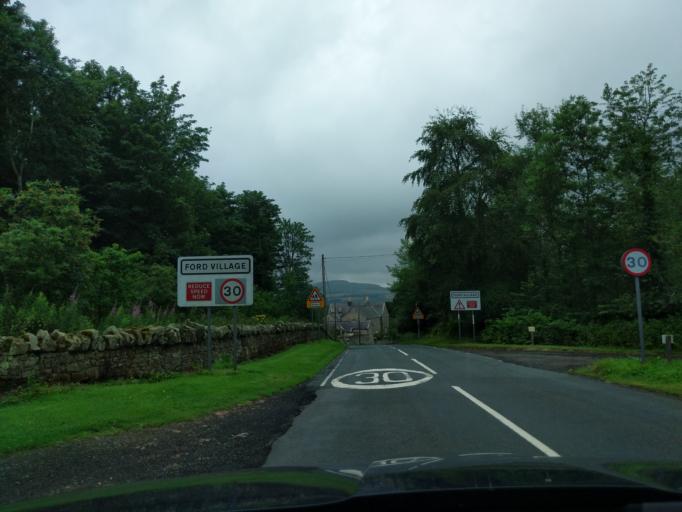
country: GB
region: England
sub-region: Northumberland
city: Ford
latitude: 55.6320
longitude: -2.0820
